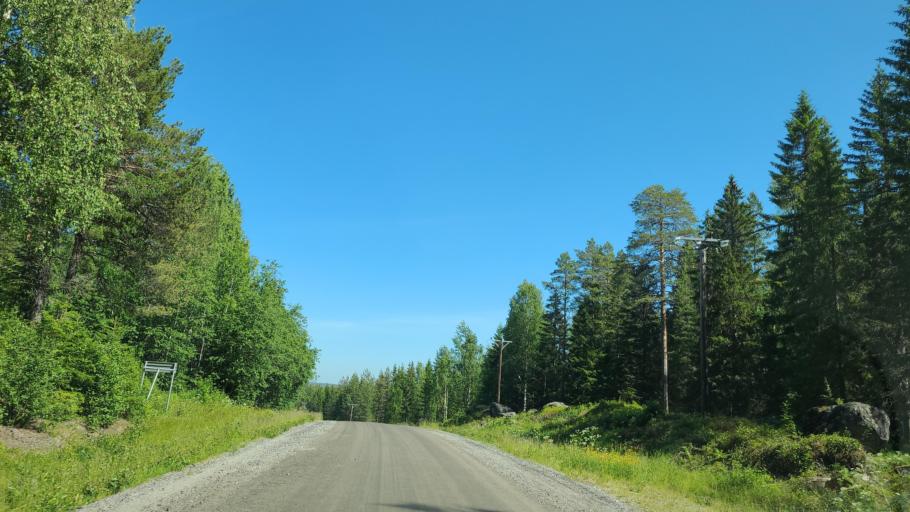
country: SE
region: Vaesterbotten
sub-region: Bjurholms Kommun
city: Bjurholm
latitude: 63.6389
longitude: 19.1961
